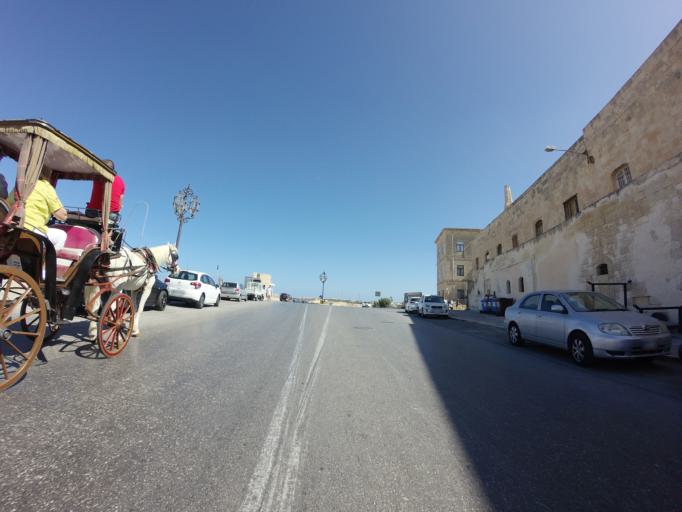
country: MT
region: Il-Belt Valletta
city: Valletta
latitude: 35.9010
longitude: 14.5181
